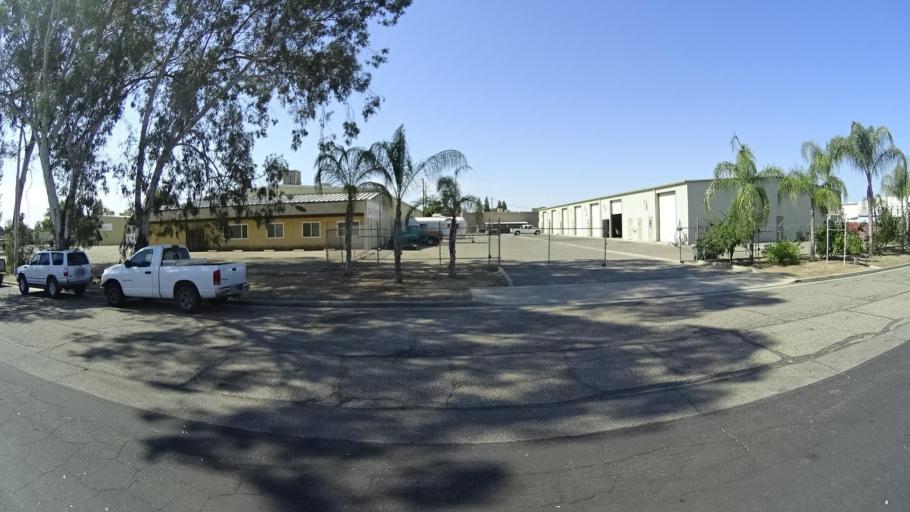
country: US
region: California
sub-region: Fresno County
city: Tarpey Village
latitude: 36.7831
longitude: -119.6932
